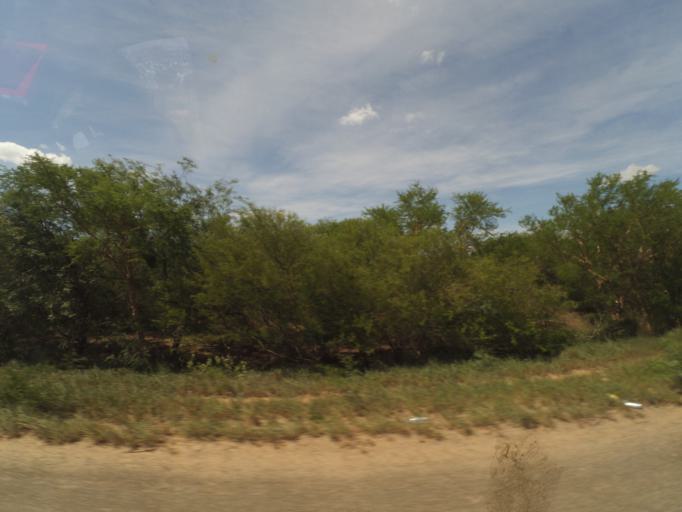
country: BO
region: Santa Cruz
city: Pailon
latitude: -17.6034
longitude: -62.2631
